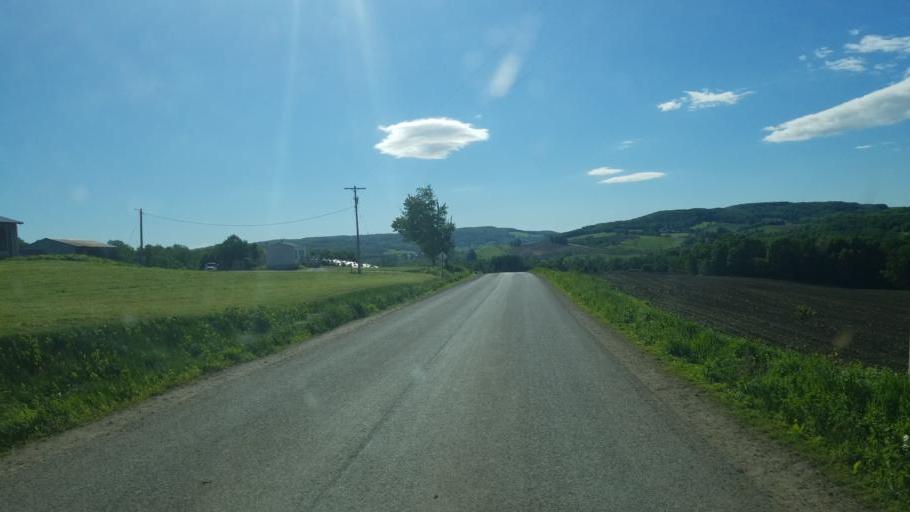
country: US
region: New York
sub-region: Herkimer County
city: Little Falls
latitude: 42.9764
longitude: -74.8035
